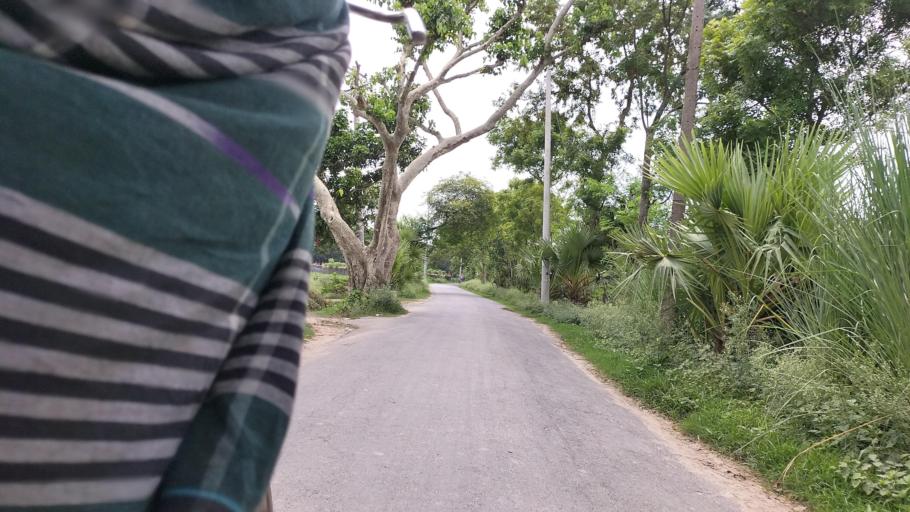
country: BD
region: Rajshahi
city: Rajshahi
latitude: 24.5141
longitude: 88.6322
